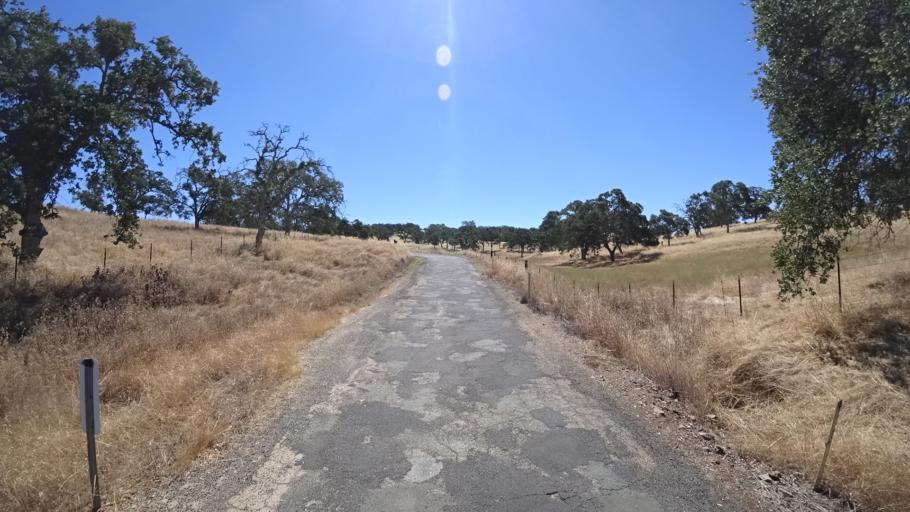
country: US
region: California
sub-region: Calaveras County
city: Rancho Calaveras
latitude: 38.0151
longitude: -120.8046
